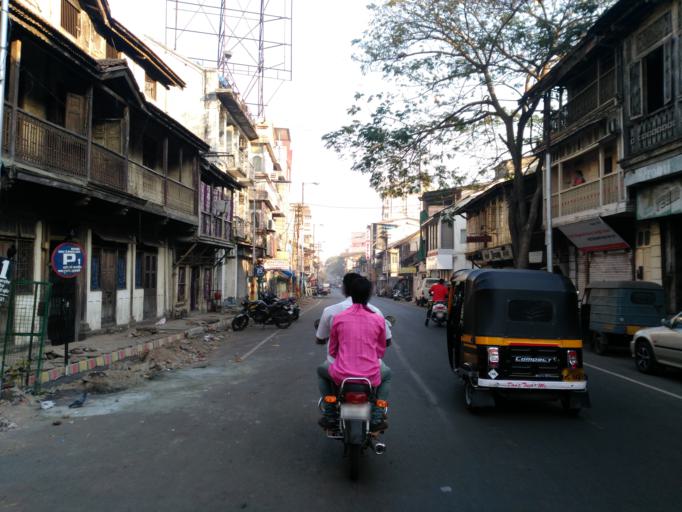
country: IN
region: Maharashtra
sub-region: Pune Division
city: Pune
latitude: 18.5085
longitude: 73.8787
